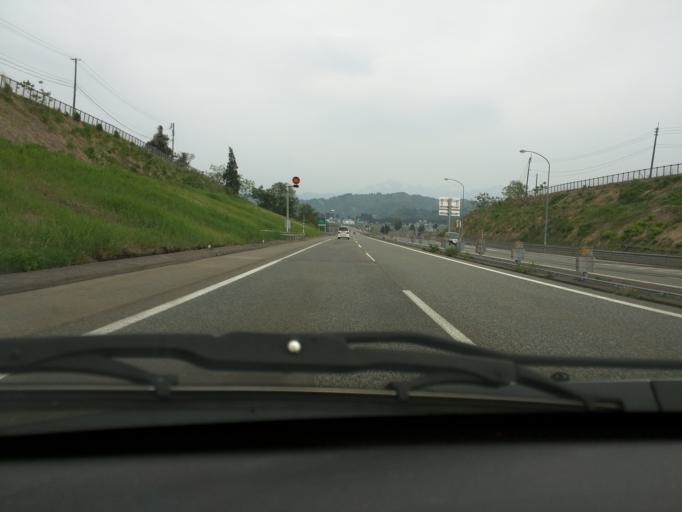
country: JP
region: Niigata
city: Ojiya
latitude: 37.2669
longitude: 138.8433
